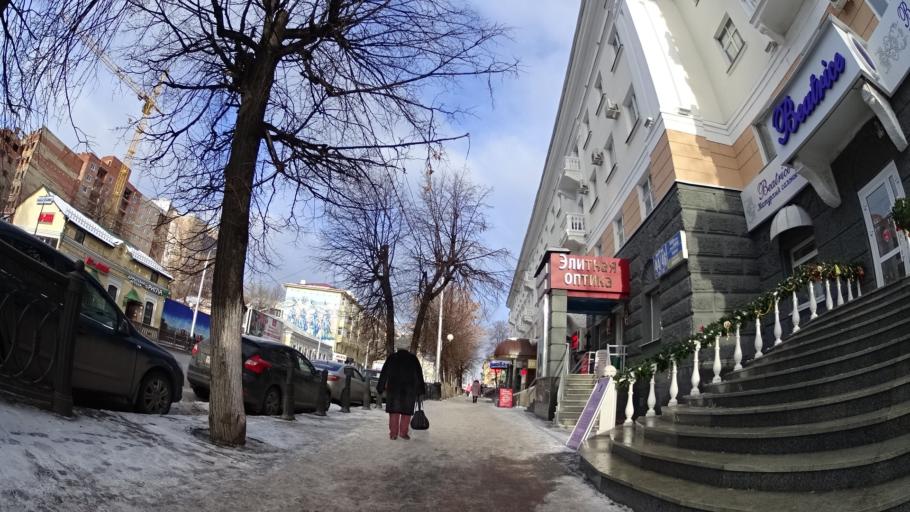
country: RU
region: Bashkortostan
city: Ufa
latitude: 54.7287
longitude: 55.9489
